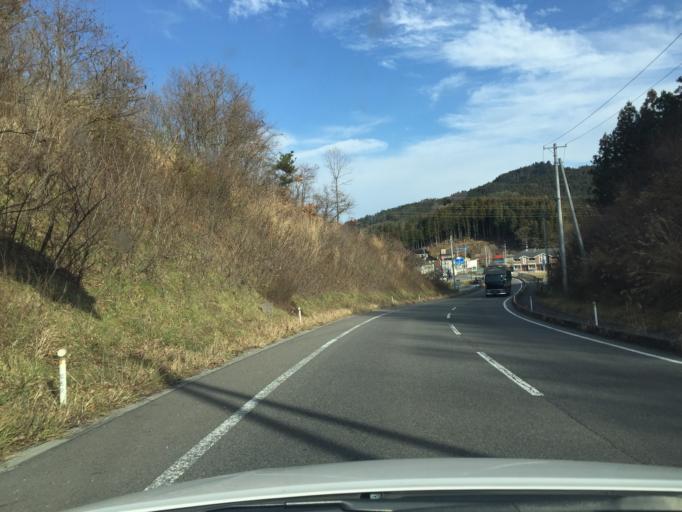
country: JP
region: Fukushima
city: Funehikimachi-funehiki
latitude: 37.2961
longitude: 140.6165
